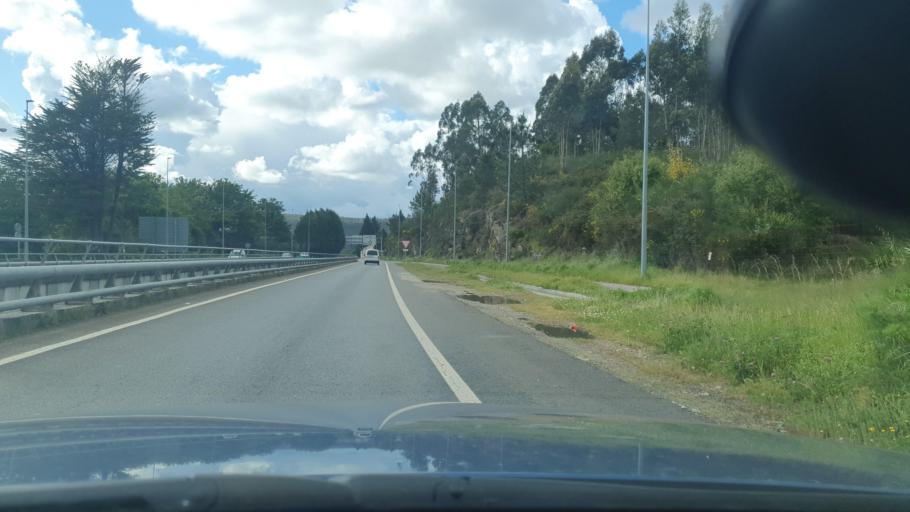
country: ES
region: Galicia
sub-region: Provincia da Coruna
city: Santiago de Compostela
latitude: 42.8698
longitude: -8.5767
